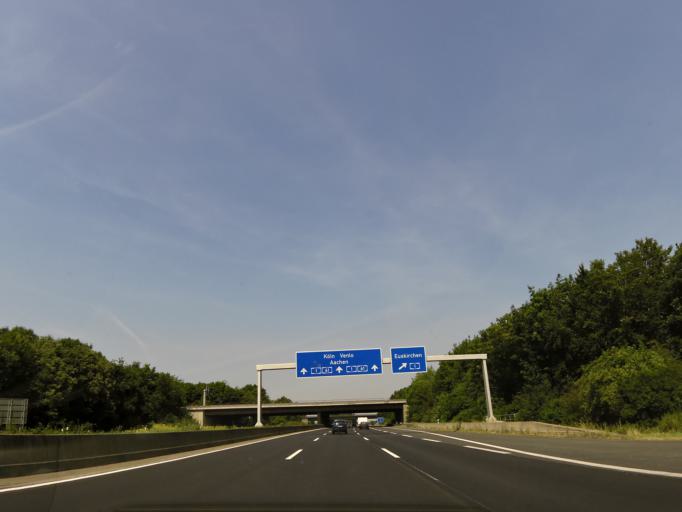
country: DE
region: North Rhine-Westphalia
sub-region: Regierungsbezirk Koln
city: Weilerswist
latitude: 50.7693
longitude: 6.8267
